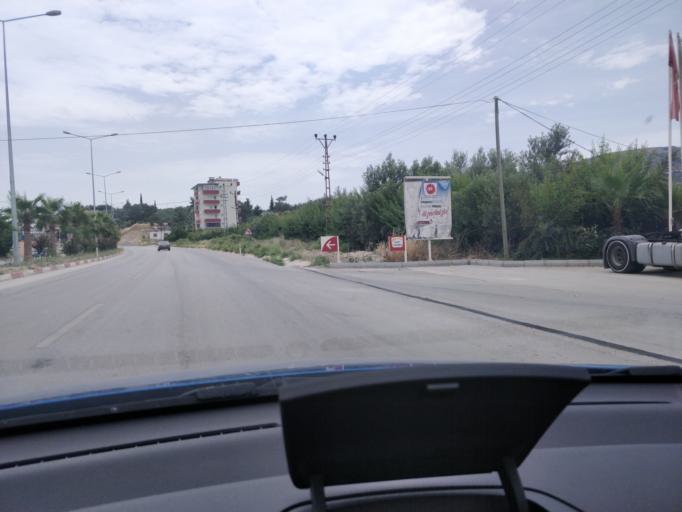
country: TR
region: Mersin
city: Mut
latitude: 36.6592
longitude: 33.4216
